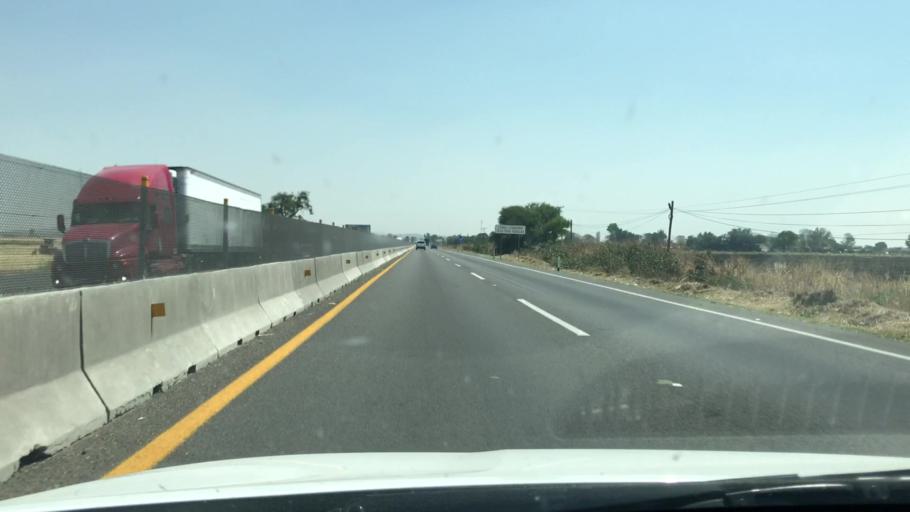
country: MX
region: Guanajuato
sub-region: Abasolo
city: San Bernardo Pena Blanca
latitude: 20.4794
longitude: -101.4969
